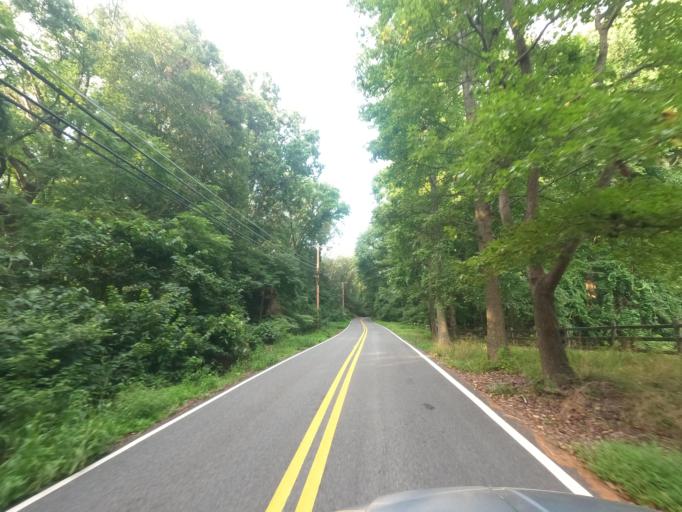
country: US
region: Maryland
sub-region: Prince George's County
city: Accokeek
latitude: 38.6842
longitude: -77.0135
